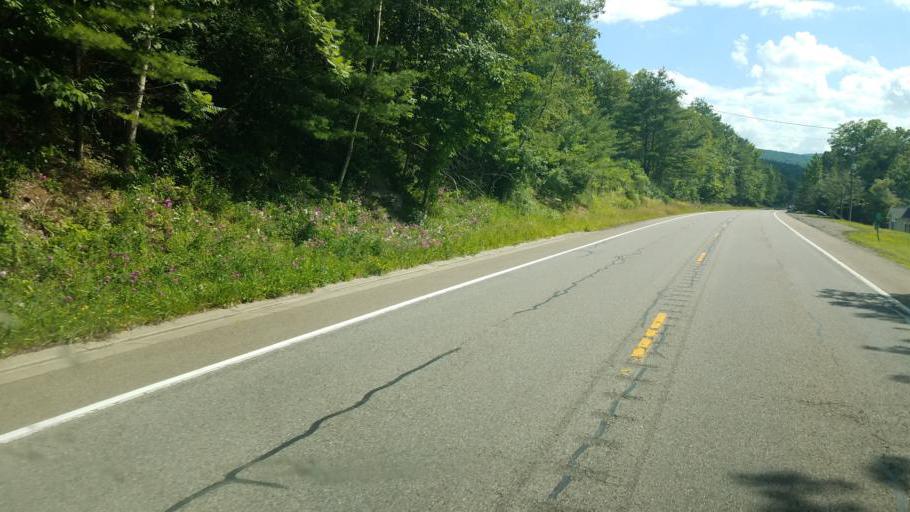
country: US
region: New York
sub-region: Steuben County
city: Sylvan Beach
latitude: 42.4253
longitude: -77.1807
